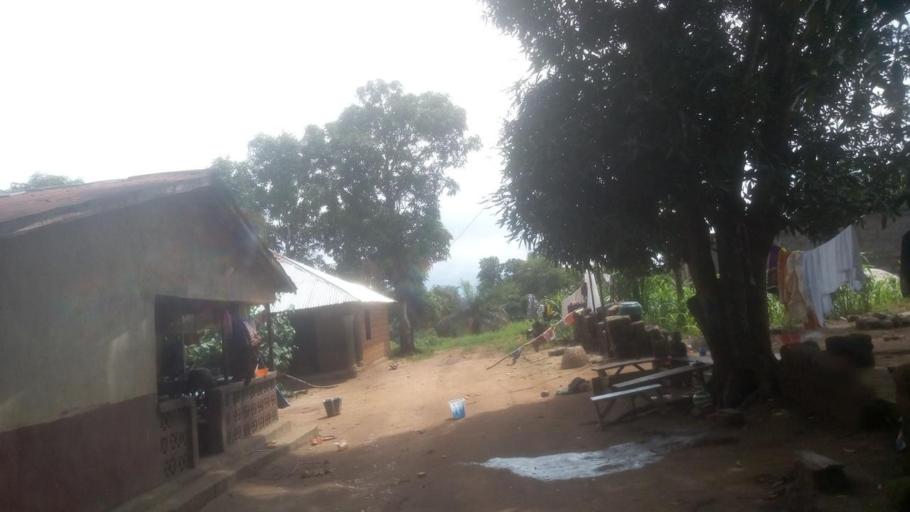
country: SL
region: Western Area
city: Freetown
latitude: 8.5293
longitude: -13.1509
